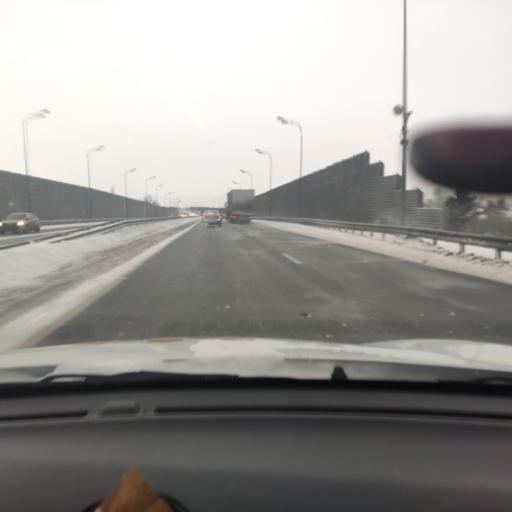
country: RU
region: Tatarstan
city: Osinovo
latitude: 55.8243
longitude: 48.8464
